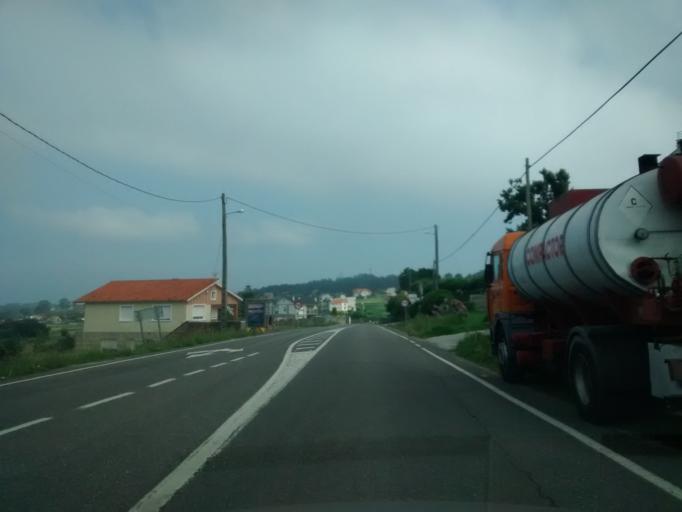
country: ES
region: Galicia
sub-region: Provincia de Pontevedra
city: Sanxenxo
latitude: 42.4053
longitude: -8.8530
